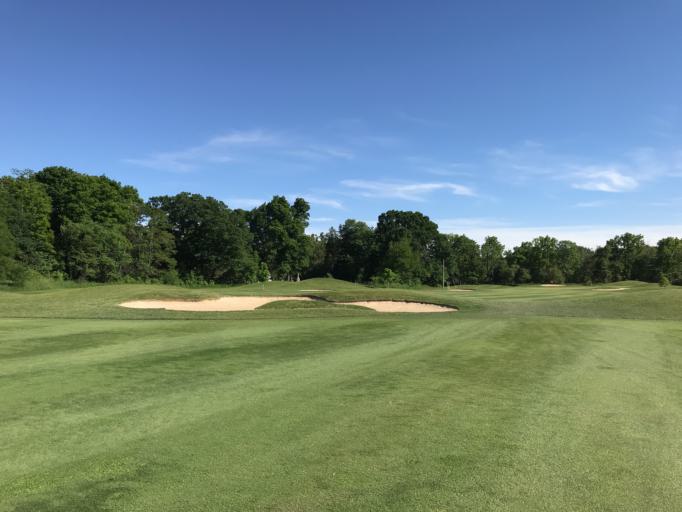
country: US
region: Michigan
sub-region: Oakland County
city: South Lyon
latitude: 42.4507
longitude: -83.5734
